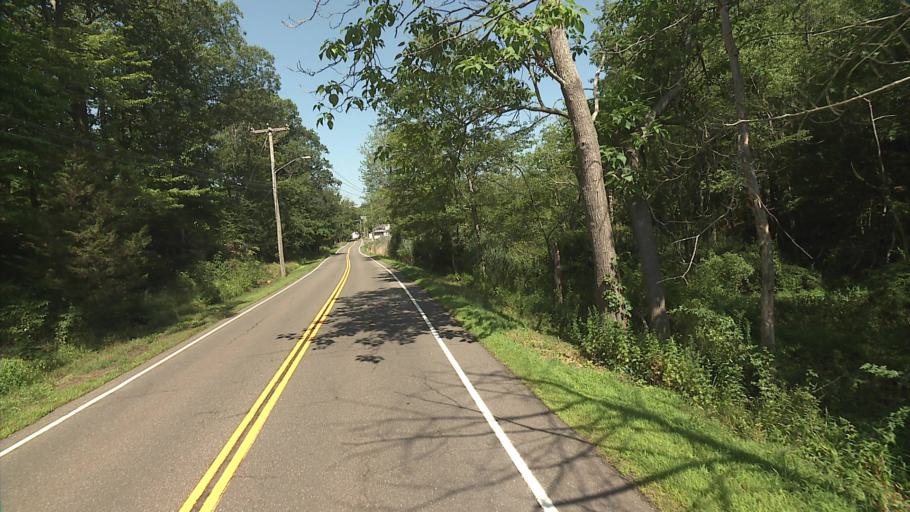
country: US
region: Connecticut
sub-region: New Haven County
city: Guilford
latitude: 41.2680
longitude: -72.7340
